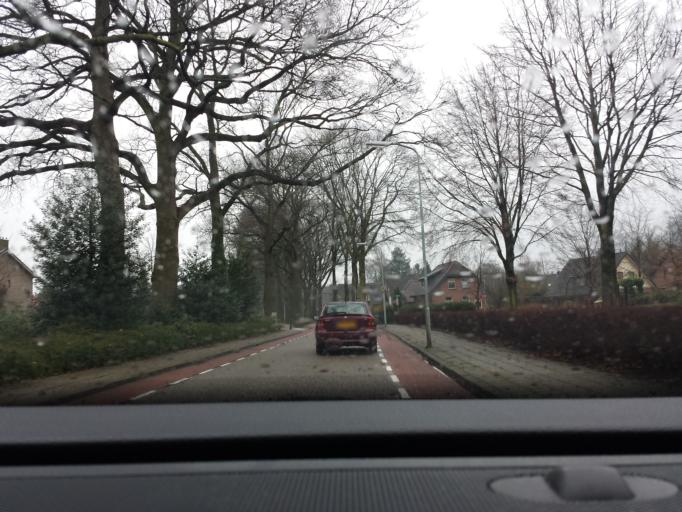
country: NL
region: Gelderland
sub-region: Gemeente Bronckhorst
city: Zelhem
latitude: 52.0087
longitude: 6.3475
